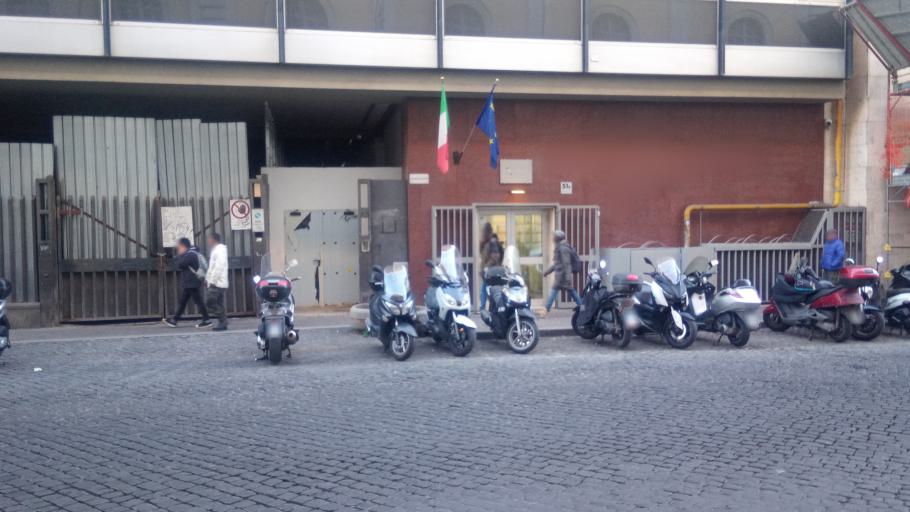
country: IT
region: Latium
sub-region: Citta metropolitana di Roma Capitale
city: Rome
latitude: 41.9008
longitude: 12.5054
